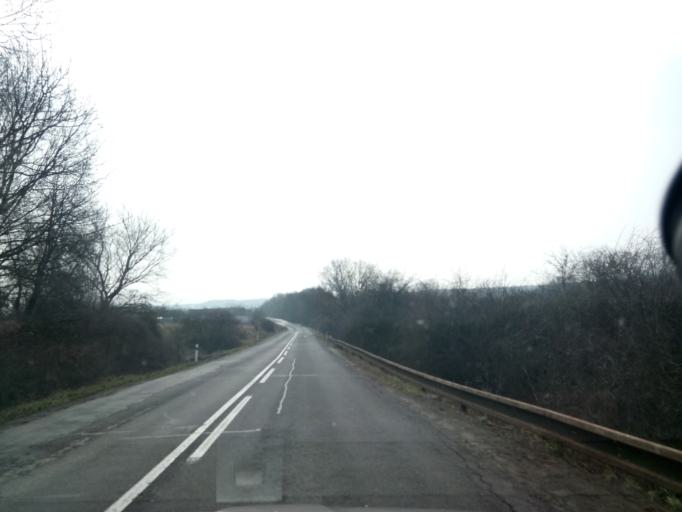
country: SK
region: Kosicky
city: Secovce
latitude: 48.6287
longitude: 21.5857
